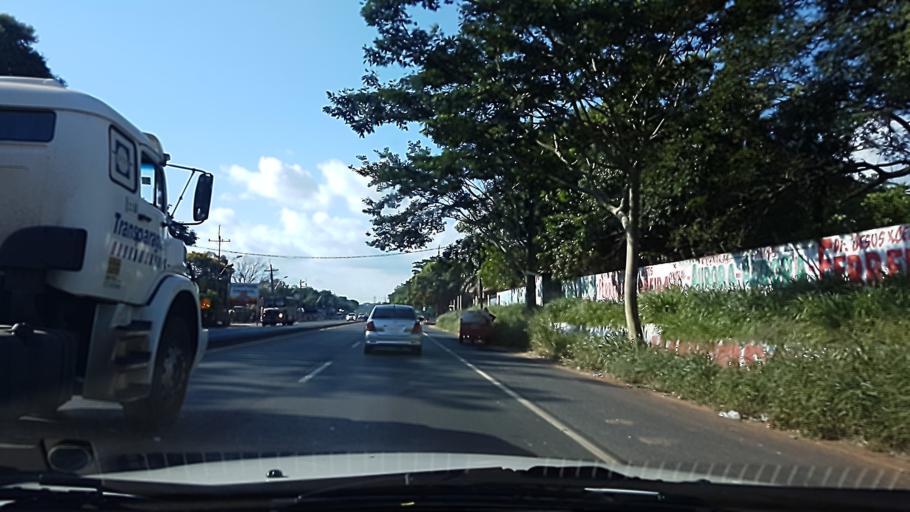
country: PY
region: Central
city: San Antonio
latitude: -25.4337
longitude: -57.5367
